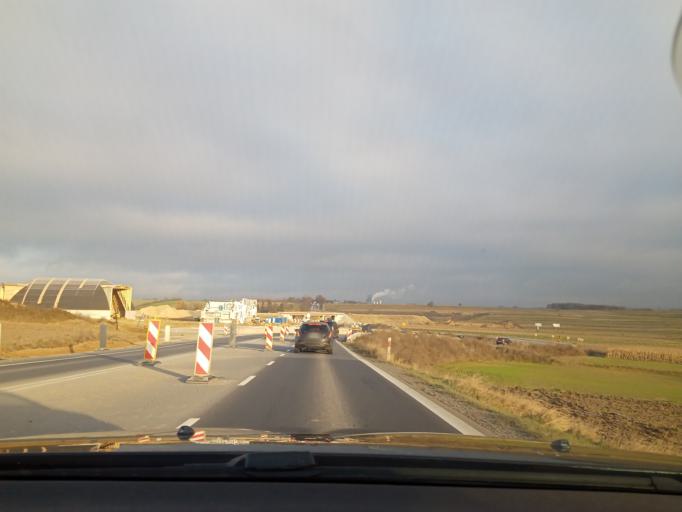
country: PL
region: Lesser Poland Voivodeship
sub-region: Powiat miechowski
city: Miechow
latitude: 50.3118
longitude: 20.0398
